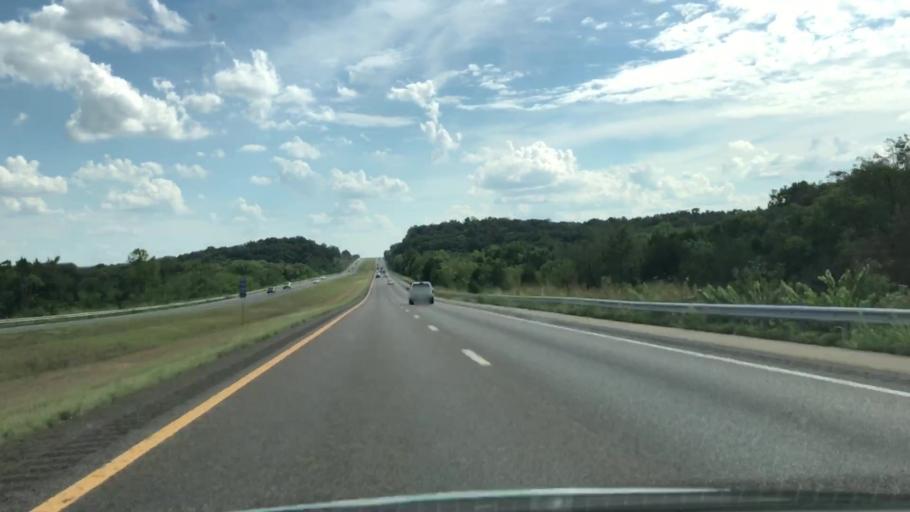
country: US
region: Tennessee
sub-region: Maury County
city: Columbia
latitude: 35.6074
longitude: -86.9011
